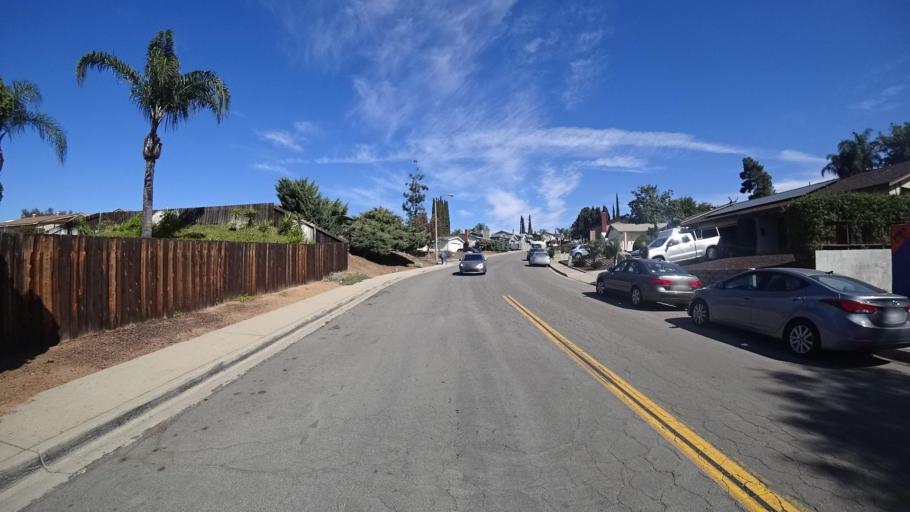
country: US
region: California
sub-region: San Diego County
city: Granite Hills
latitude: 32.8312
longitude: -116.8949
